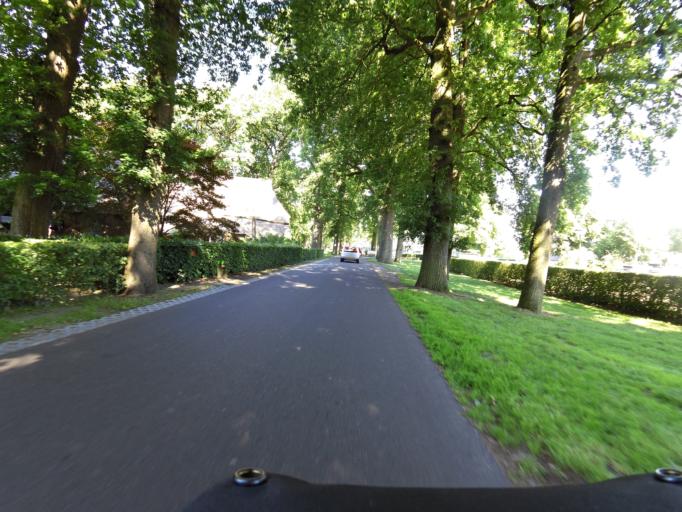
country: NL
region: Overijssel
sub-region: Gemeente Dalfsen
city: Dalfsen
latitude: 52.5103
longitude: 6.3530
